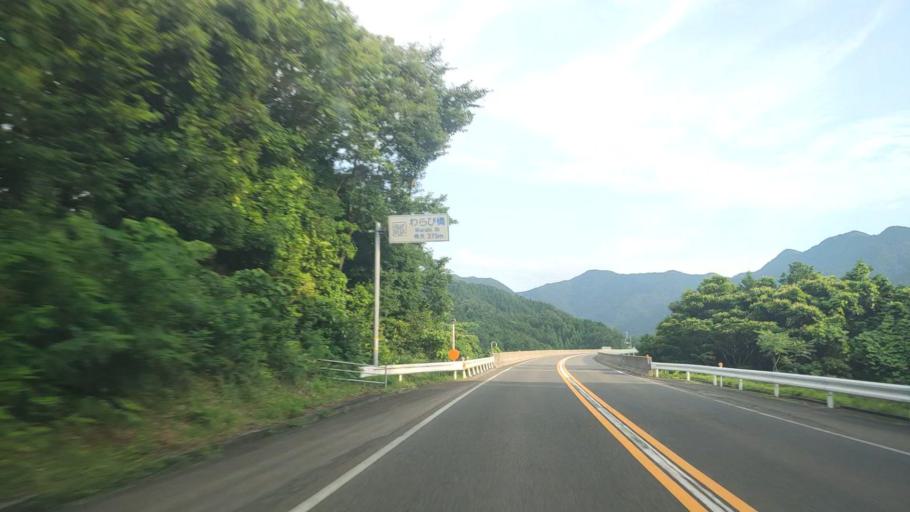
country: JP
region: Tottori
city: Kurayoshi
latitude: 35.3342
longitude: 133.7549
